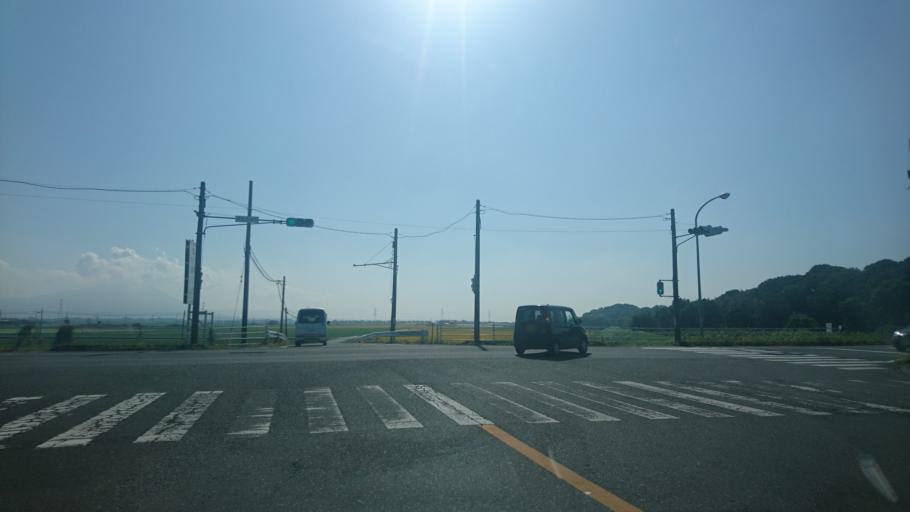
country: JP
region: Ibaraki
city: Shimodate
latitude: 36.2785
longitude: 139.9719
